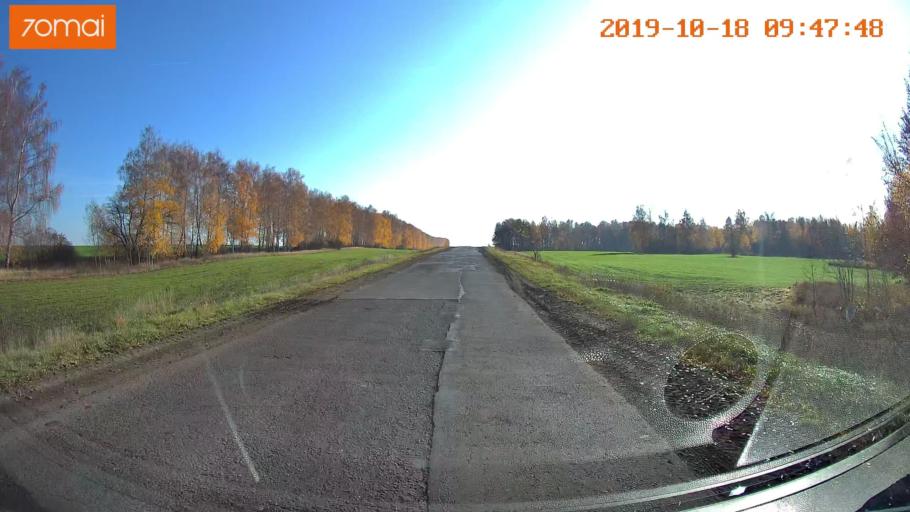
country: RU
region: Tula
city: Kazachka
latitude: 53.3203
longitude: 38.2367
